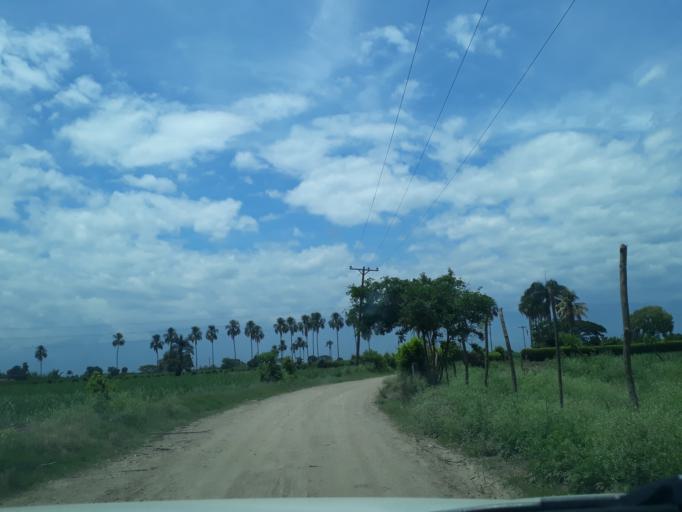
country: CO
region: Valle del Cauca
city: Cali
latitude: 3.3677
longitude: -76.4771
